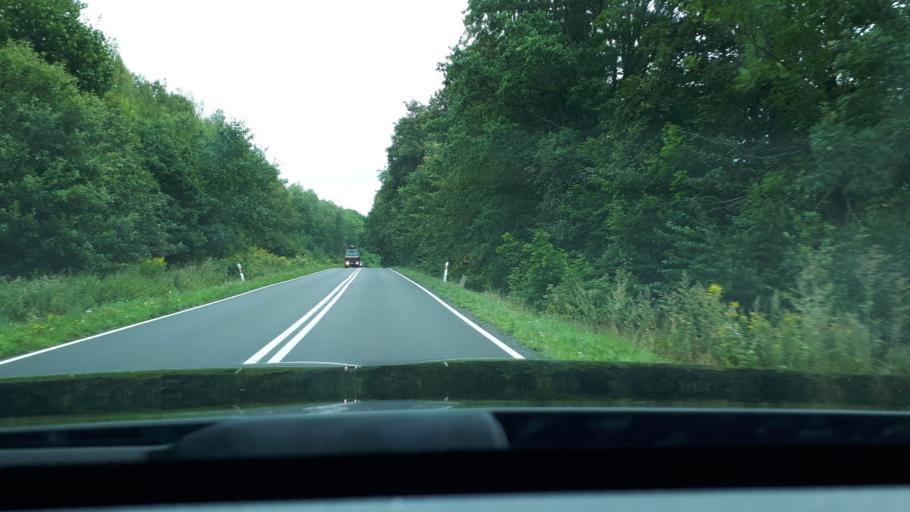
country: PL
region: Lower Silesian Voivodeship
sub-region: Powiat lwowecki
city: Lwowek Slaski
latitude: 51.1201
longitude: 15.6260
